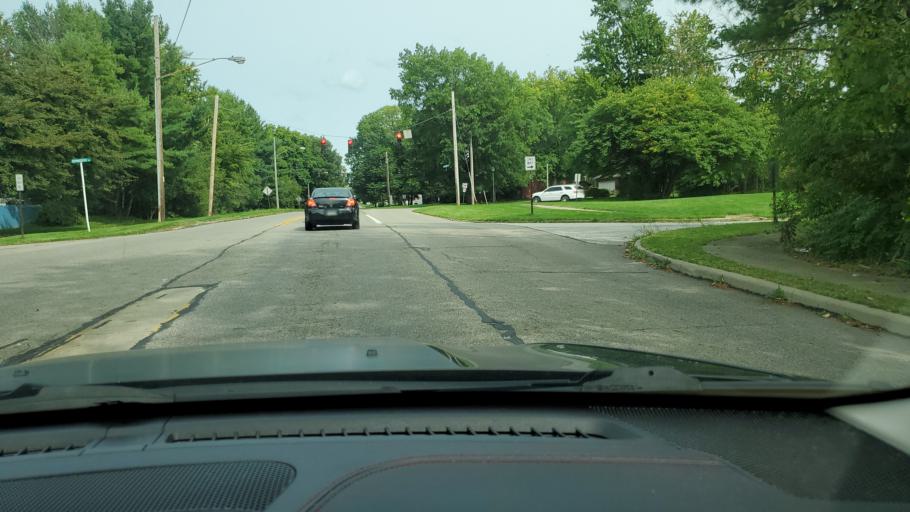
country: US
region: Ohio
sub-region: Mahoning County
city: Boardman
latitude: 41.0536
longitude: -80.6723
